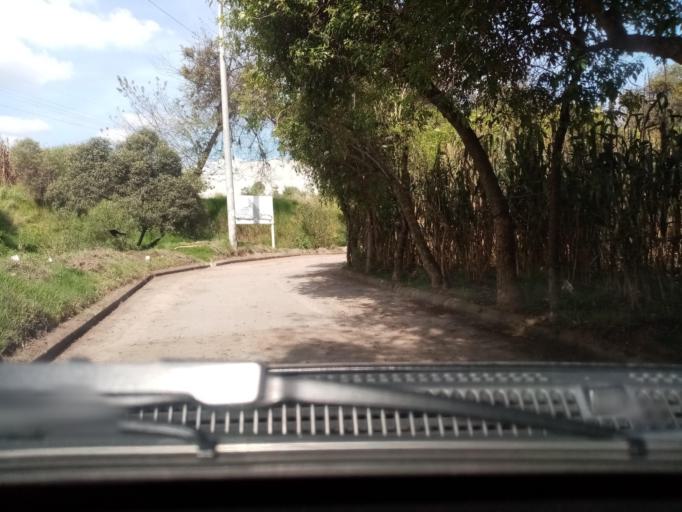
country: GT
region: Quetzaltenango
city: Quetzaltenango
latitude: 14.8582
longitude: -91.5307
